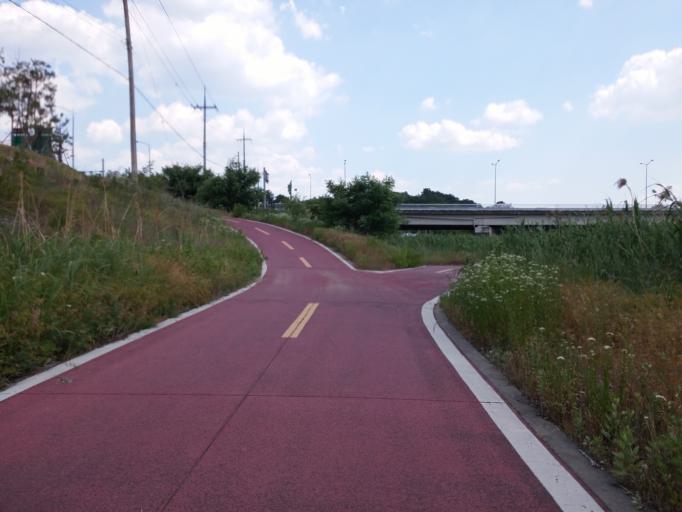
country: KR
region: Chungcheongbuk-do
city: Cheongju-si
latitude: 36.5641
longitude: 127.5094
